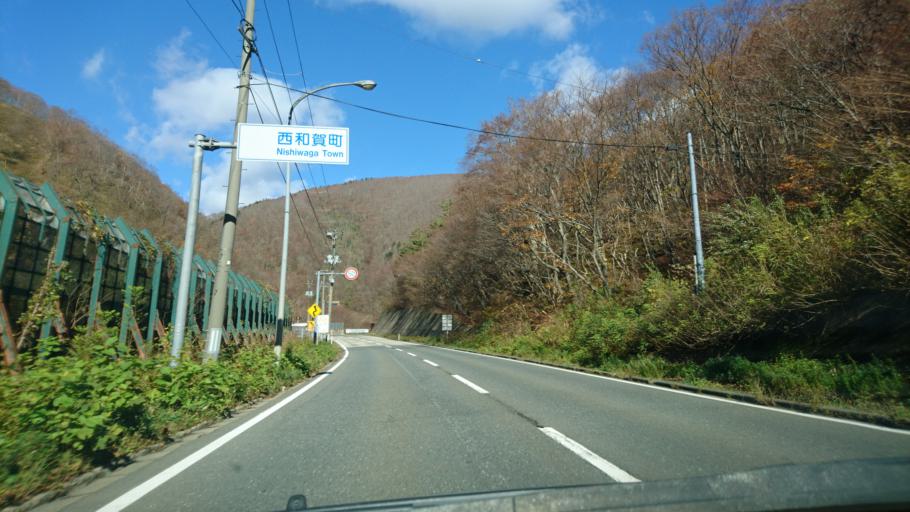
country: JP
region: Iwate
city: Kitakami
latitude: 39.3051
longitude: 140.8926
